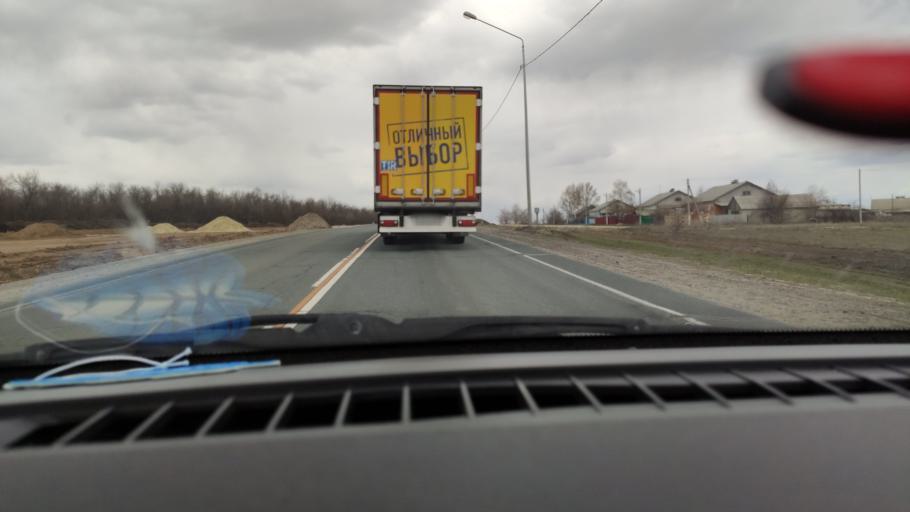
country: RU
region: Saratov
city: Sennoy
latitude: 52.1591
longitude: 47.0611
